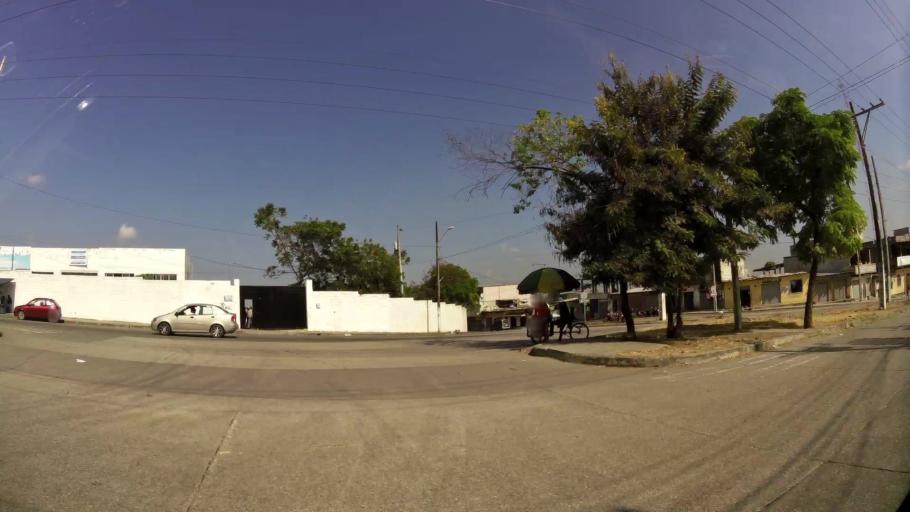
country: EC
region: Guayas
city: Eloy Alfaro
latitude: -2.1727
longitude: -79.8059
